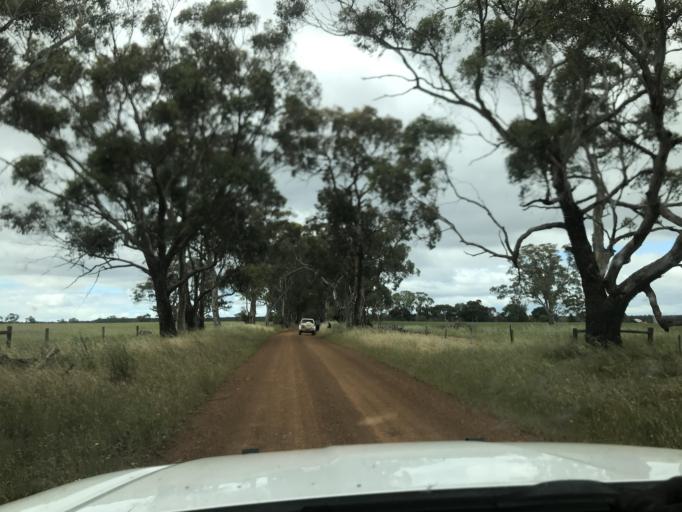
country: AU
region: South Australia
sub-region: Wattle Range
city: Penola
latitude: -37.1080
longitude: 141.2289
